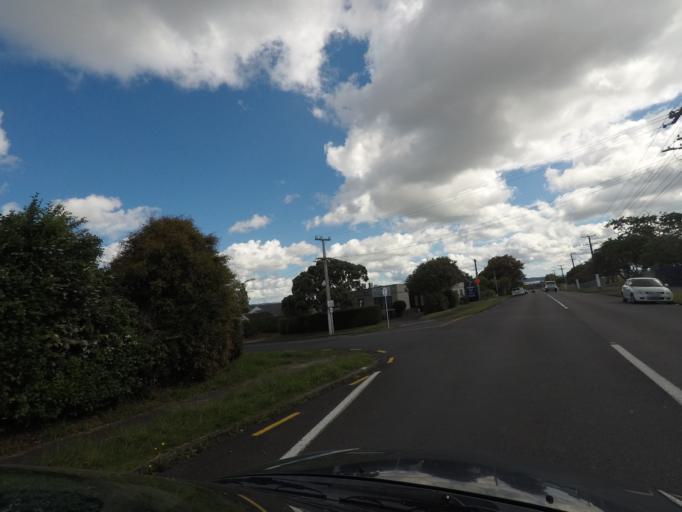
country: NZ
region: Auckland
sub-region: Auckland
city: Waitakere
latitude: -36.9061
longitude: 174.6636
